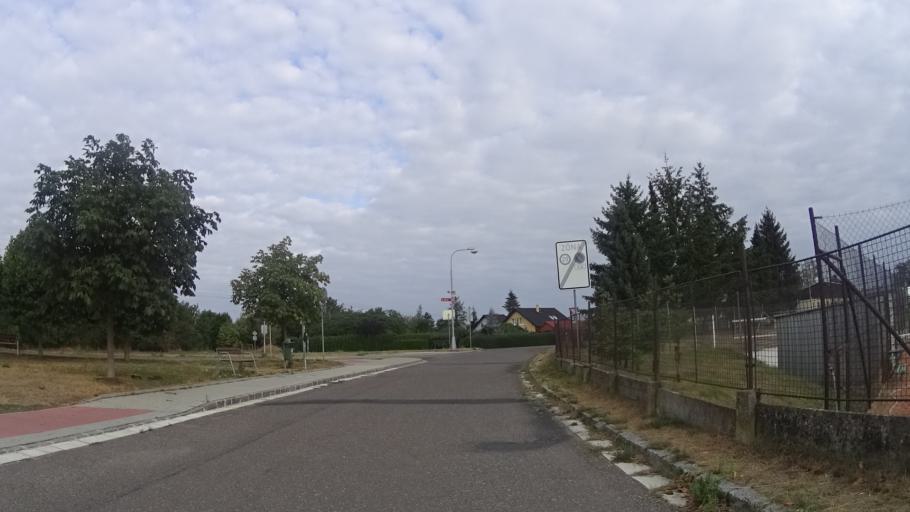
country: CZ
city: Stezery
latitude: 50.2123
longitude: 15.7470
